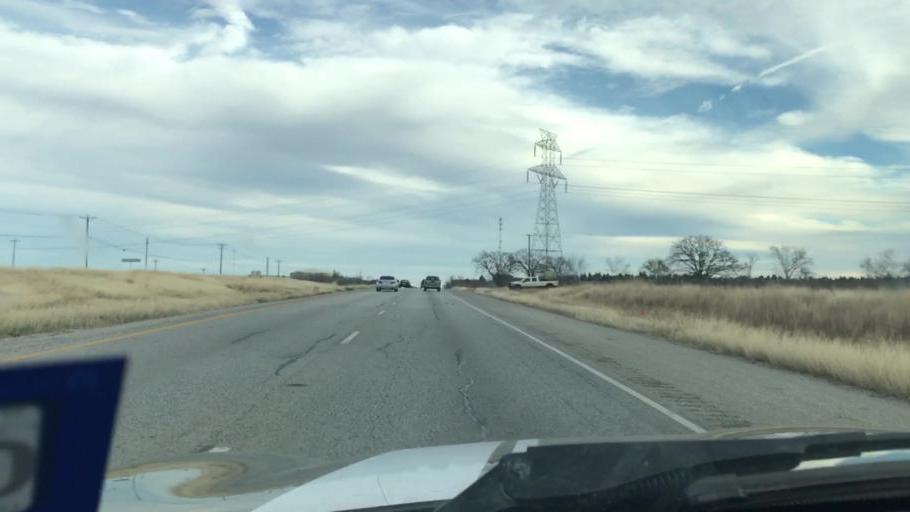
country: US
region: Texas
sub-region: Bastrop County
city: Elgin
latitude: 30.3310
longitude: -97.3483
